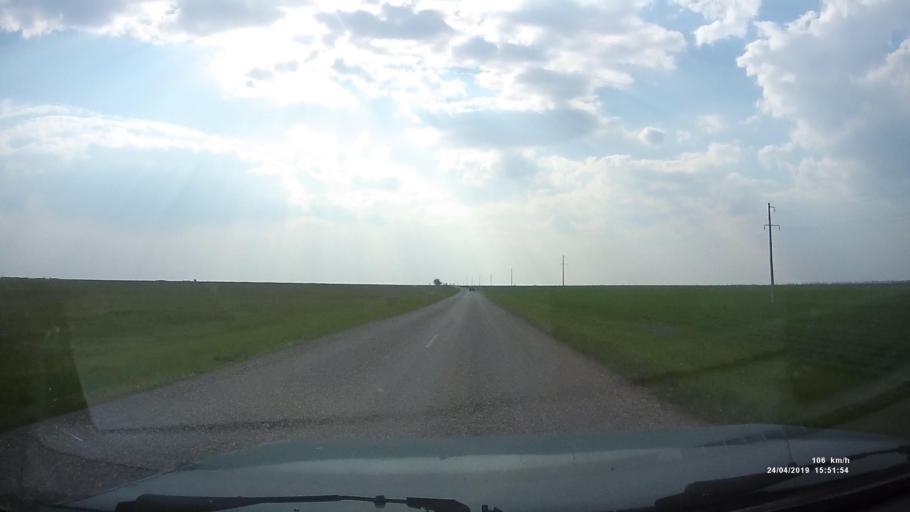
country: RU
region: Kalmykiya
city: Yashalta
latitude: 46.6045
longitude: 42.6000
